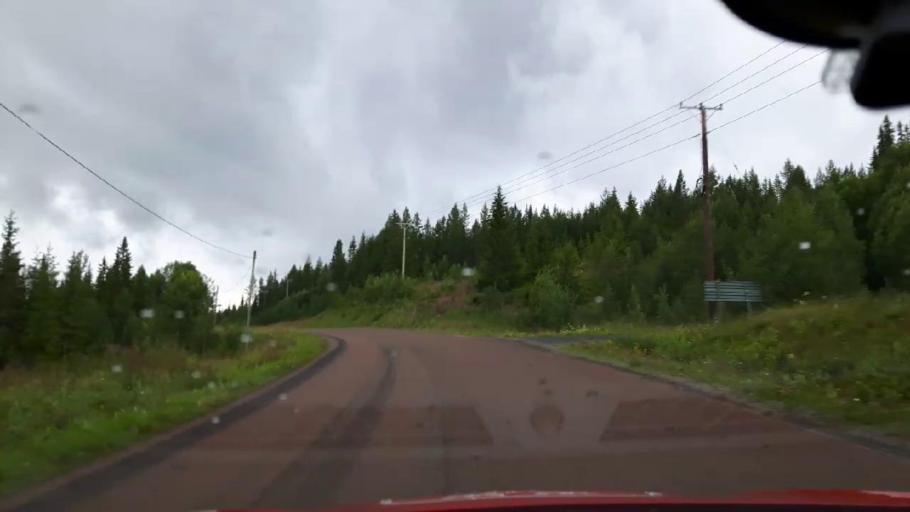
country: SE
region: Jaemtland
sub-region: Are Kommun
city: Jarpen
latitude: 63.3278
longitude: 13.6934
